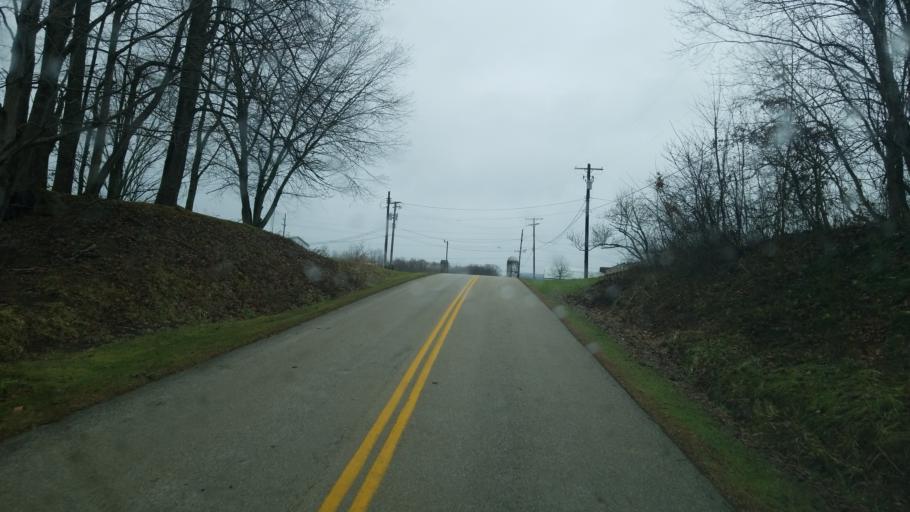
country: US
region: Ohio
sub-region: Ashtabula County
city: Roaming Shores
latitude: 41.7097
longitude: -80.8545
